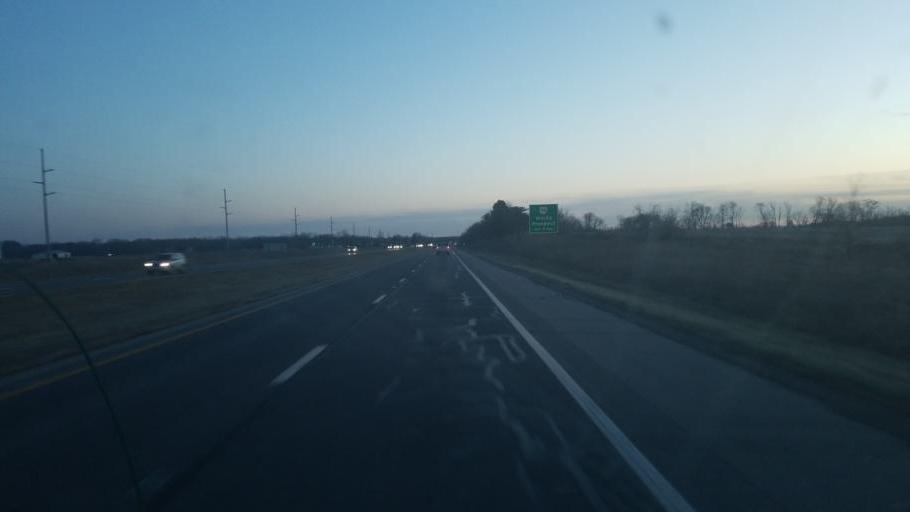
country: US
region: Ohio
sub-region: Marion County
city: Prospect
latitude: 40.4806
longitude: -83.0748
